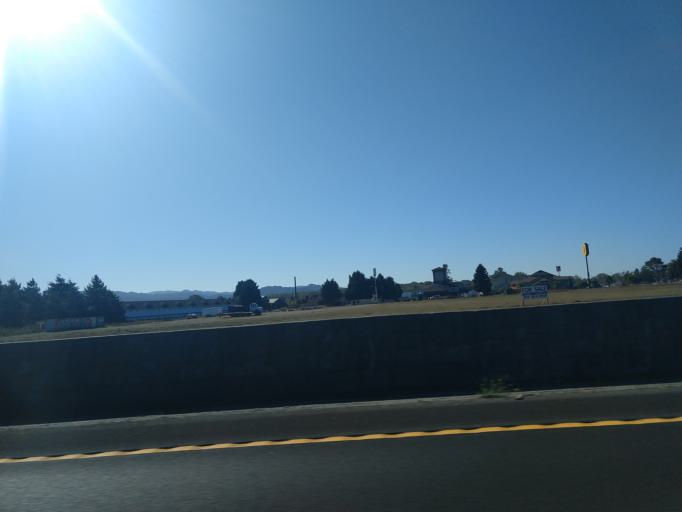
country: US
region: California
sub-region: Humboldt County
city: Fortuna
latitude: 40.5785
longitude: -124.1498
